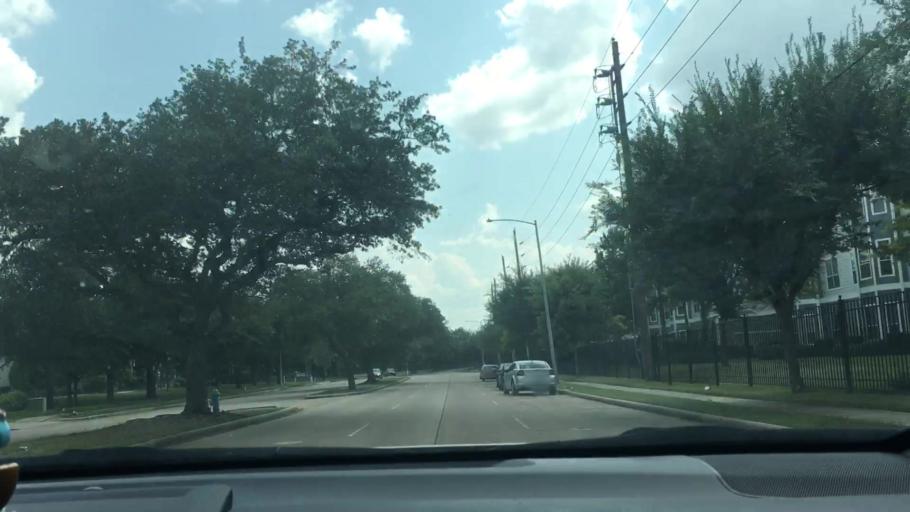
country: US
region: Texas
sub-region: Fort Bend County
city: Mission Bend
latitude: 29.7335
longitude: -95.6366
